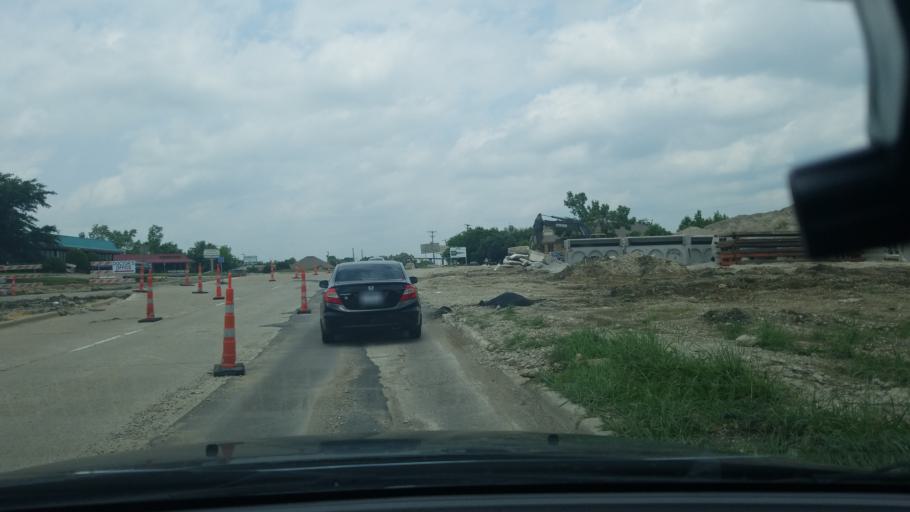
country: US
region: Texas
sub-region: Dallas County
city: Mesquite
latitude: 32.7964
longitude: -96.6340
